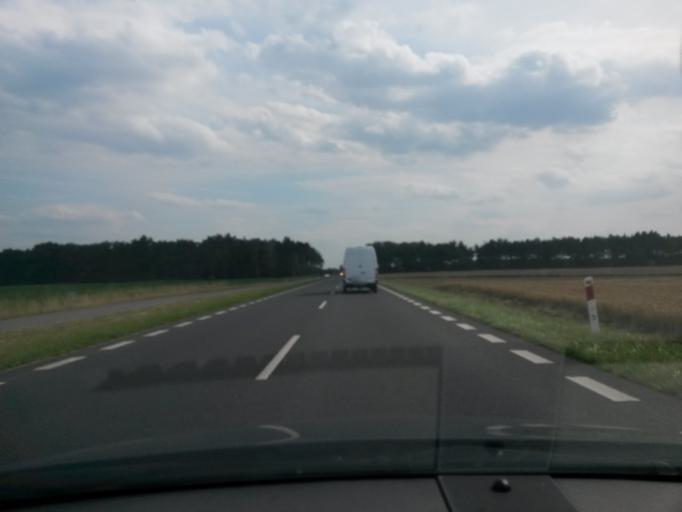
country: PL
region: Greater Poland Voivodeship
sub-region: Powiat sremski
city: Srem
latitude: 52.1174
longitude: 17.0437
